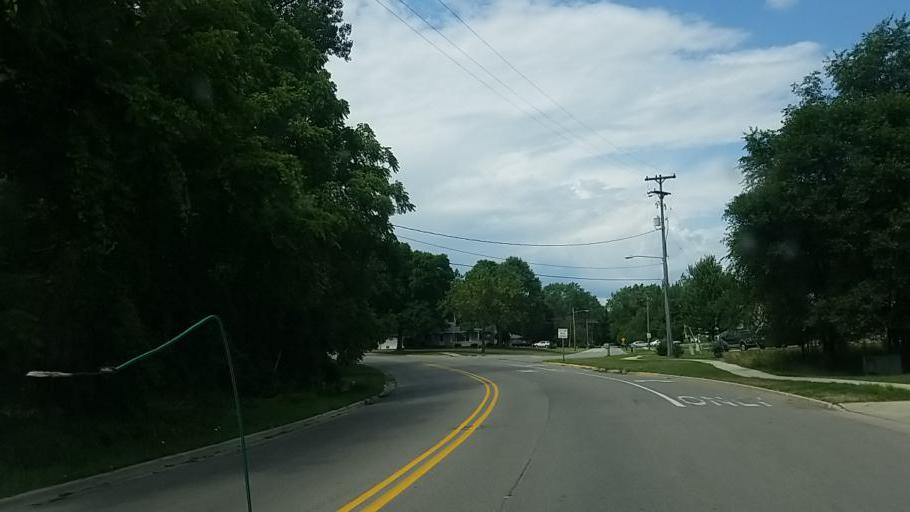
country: US
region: Michigan
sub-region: Kent County
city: Walker
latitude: 42.9945
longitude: -85.7275
